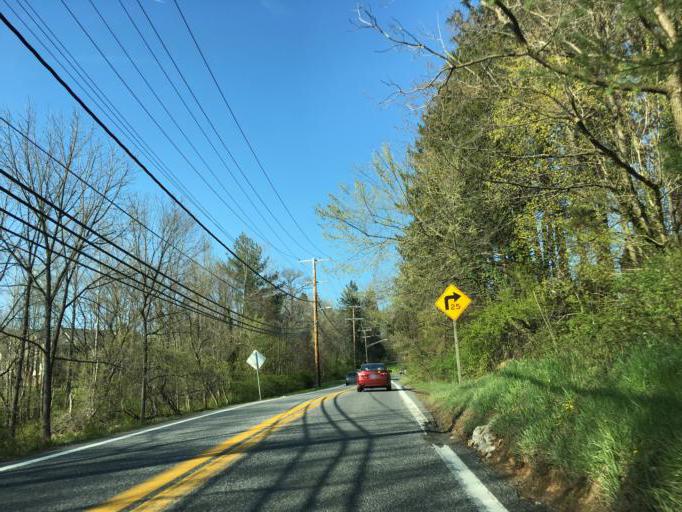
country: US
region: Maryland
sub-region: Baltimore County
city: Hunt Valley
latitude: 39.4965
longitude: -76.6426
